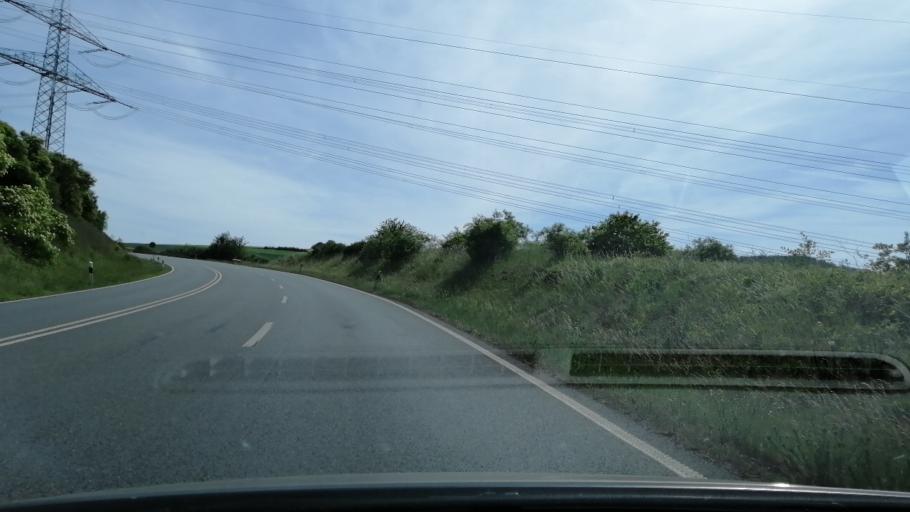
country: DE
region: Hesse
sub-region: Regierungsbezirk Kassel
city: Bad Wildungen
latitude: 51.1492
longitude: 9.1171
